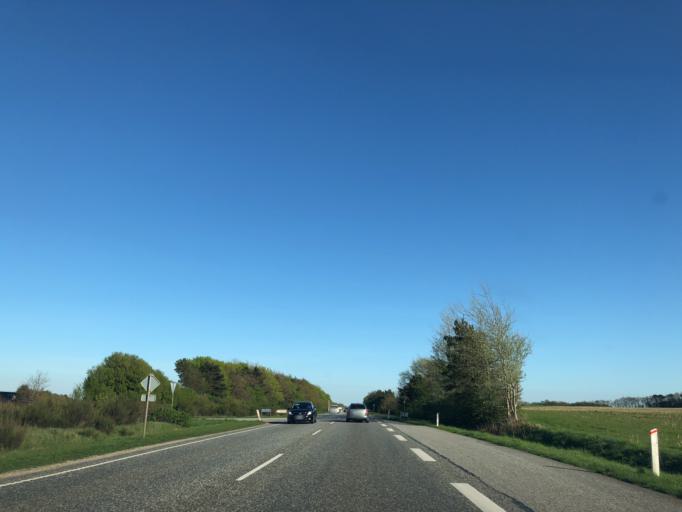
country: DK
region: Central Jutland
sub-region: Herning Kommune
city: Avlum
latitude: 56.3003
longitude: 8.7153
